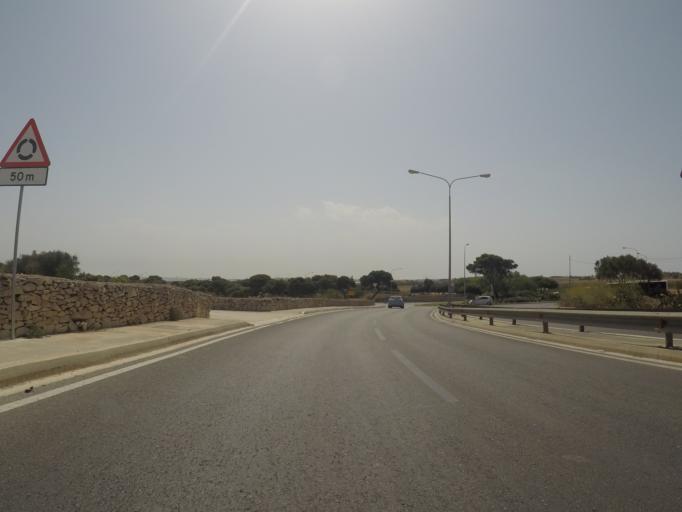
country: MT
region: L-Imdina
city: Imdina
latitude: 35.8843
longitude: 14.4148
